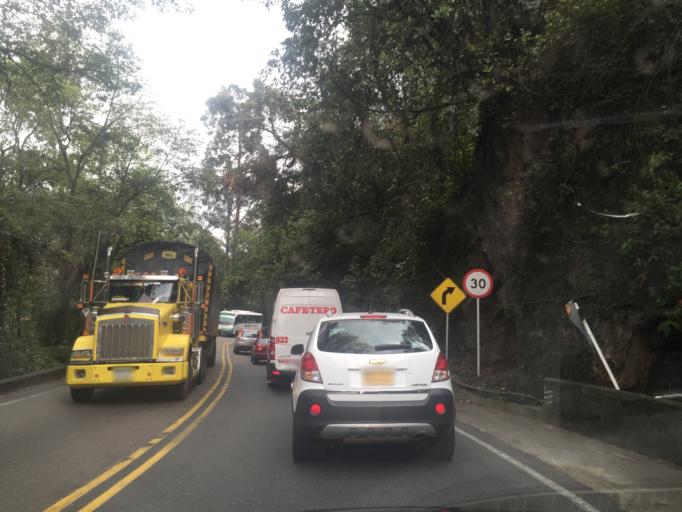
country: CO
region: Tolima
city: Cajamarca
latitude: 4.4340
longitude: -75.4602
